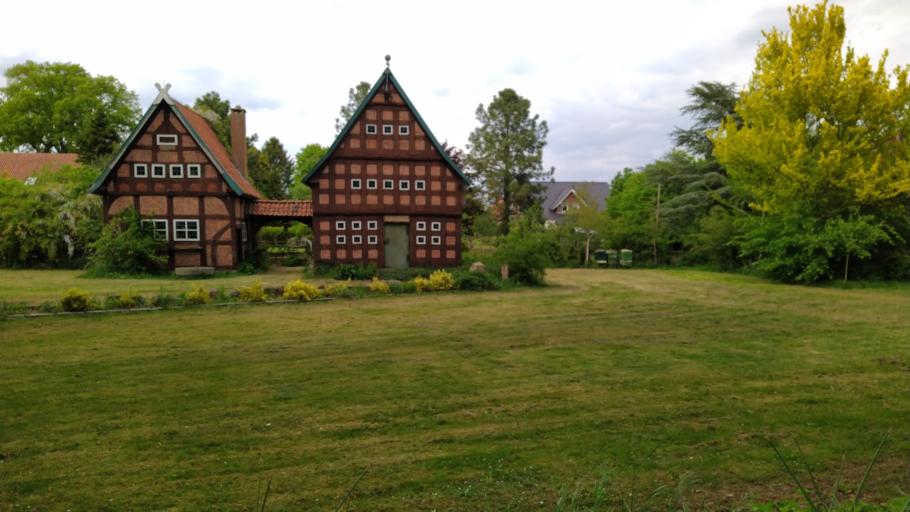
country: DE
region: Lower Saxony
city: Tarmstedt
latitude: 53.2208
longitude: 9.0693
